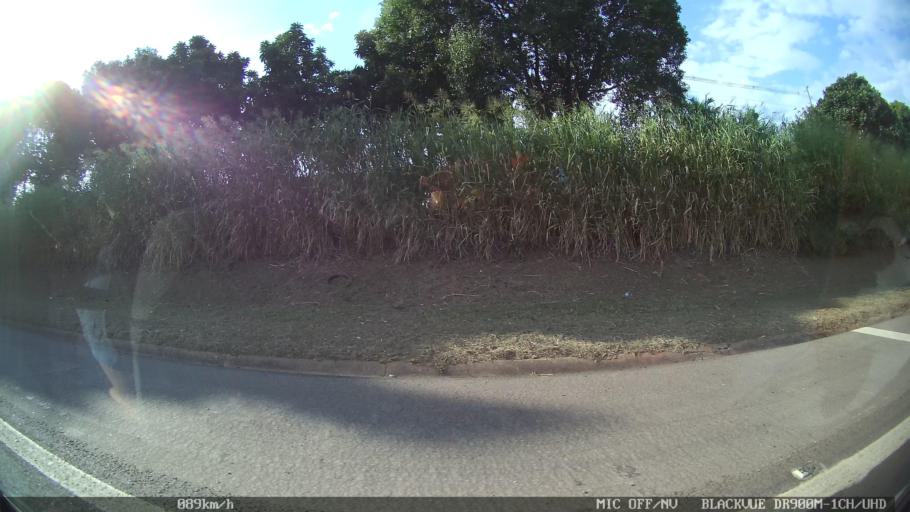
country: BR
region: Sao Paulo
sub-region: Cosmopolis
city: Cosmopolis
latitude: -22.6534
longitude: -47.1857
